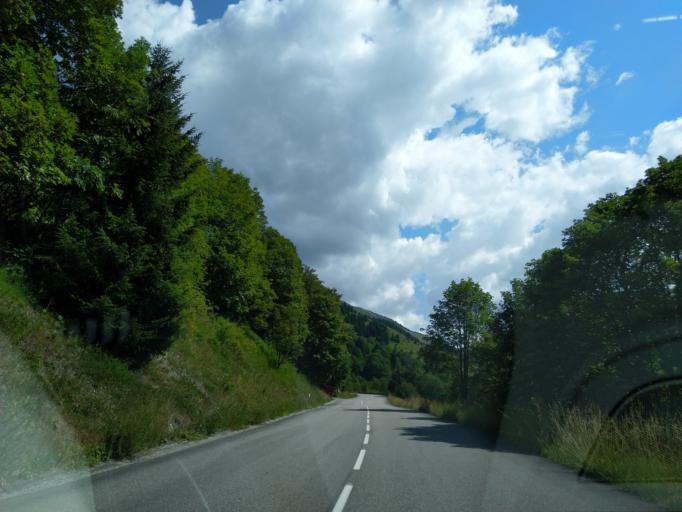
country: FR
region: Rhone-Alpes
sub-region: Departement de la Savoie
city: Meribel
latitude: 45.3869
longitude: 6.5708
